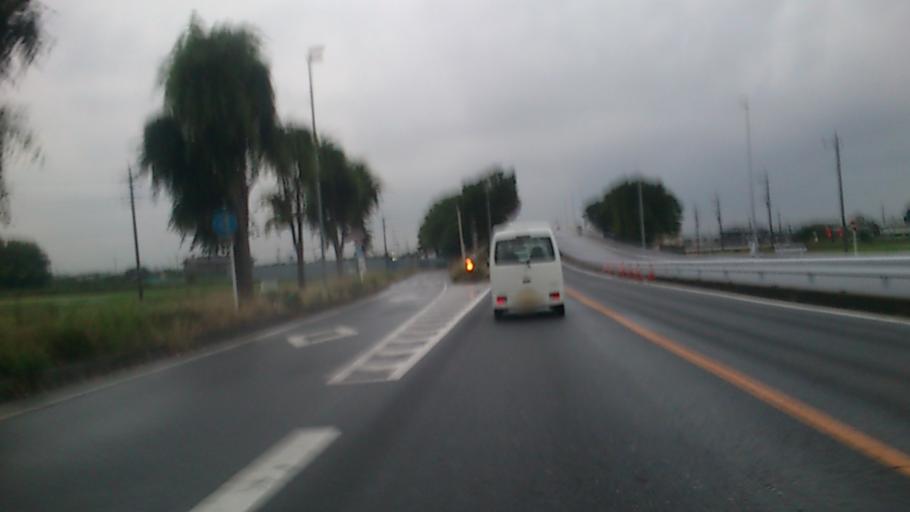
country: JP
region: Saitama
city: Gyoda
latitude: 36.1571
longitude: 139.4838
